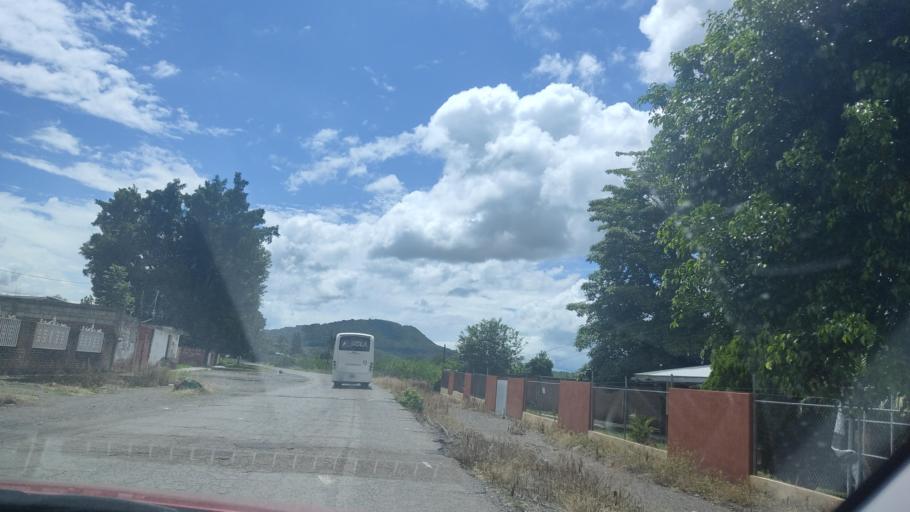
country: MX
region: Nayarit
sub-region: Ahuacatlan
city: Ahuacatlan
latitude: 21.1259
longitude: -104.6174
